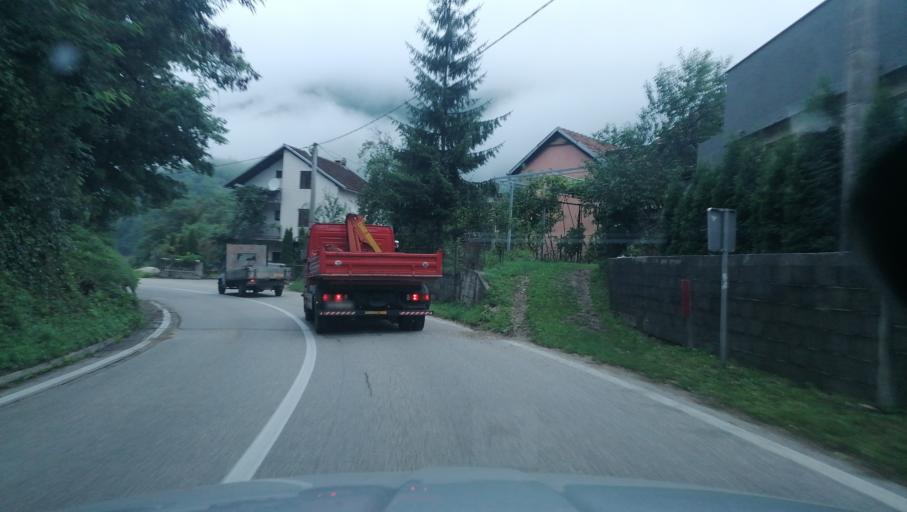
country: BA
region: Federation of Bosnia and Herzegovina
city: Jablanica
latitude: 43.7267
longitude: 17.6951
